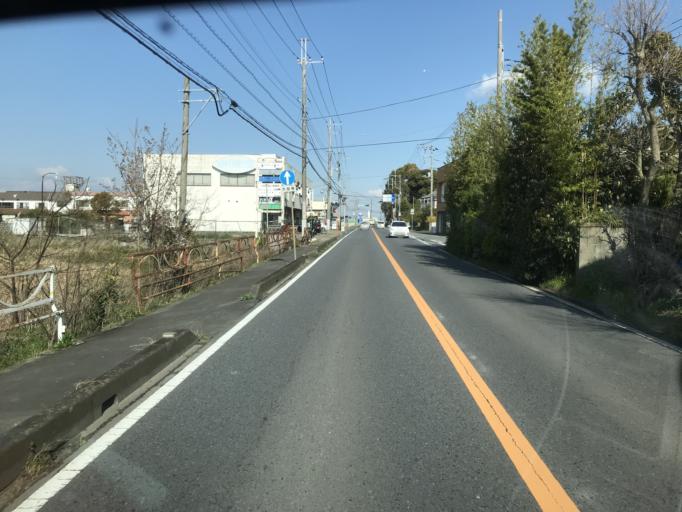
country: JP
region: Ibaraki
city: Itako
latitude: 35.9886
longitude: 140.4790
